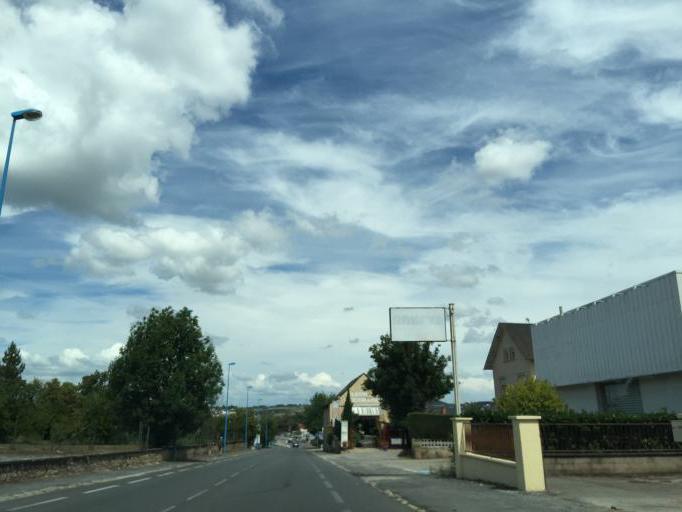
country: FR
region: Midi-Pyrenees
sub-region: Departement de l'Aveyron
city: Rodez
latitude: 44.3672
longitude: 2.5874
